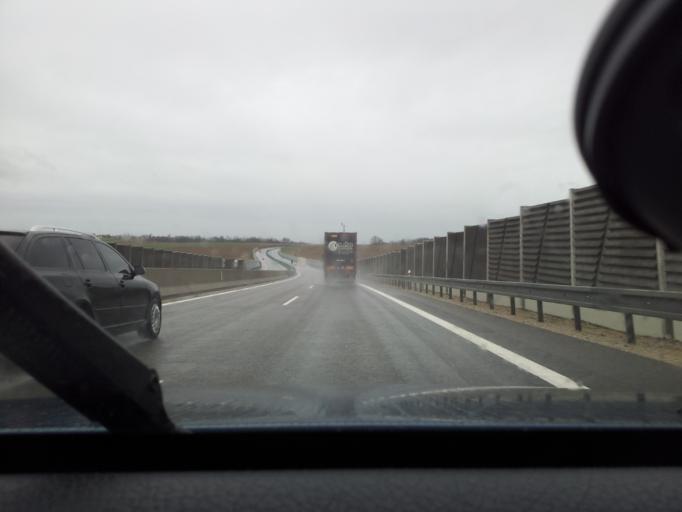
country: SK
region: Nitriansky
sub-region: Okres Nitra
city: Nitra
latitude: 48.3247
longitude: 18.1996
